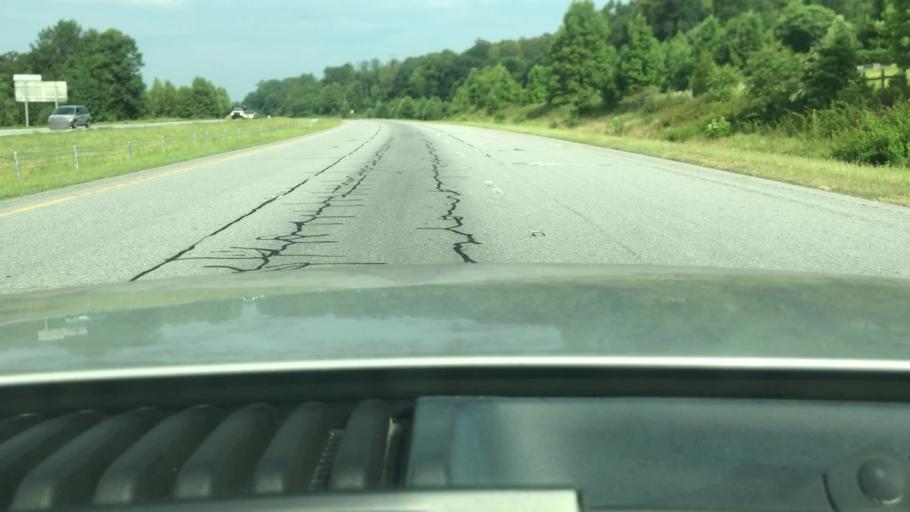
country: US
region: North Carolina
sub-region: Yadkin County
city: Jonesville
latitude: 36.1459
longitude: -80.9013
